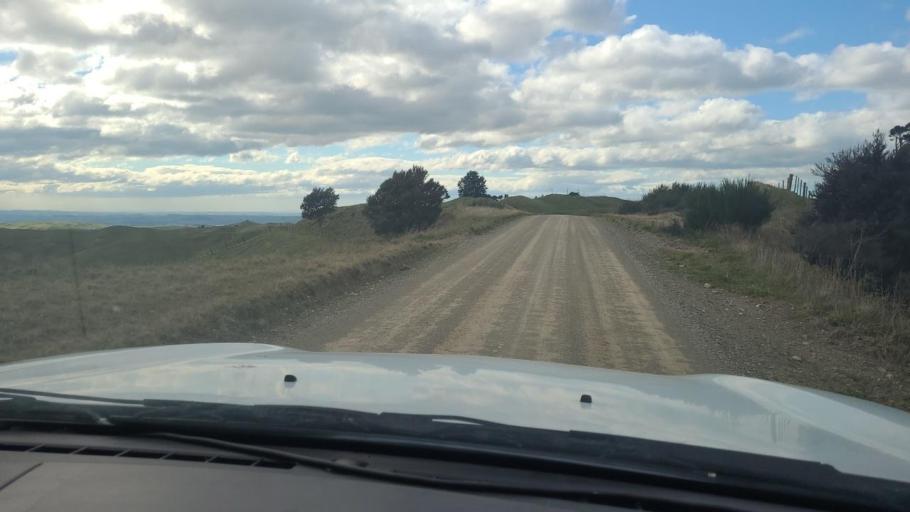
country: NZ
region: Hawke's Bay
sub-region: Hastings District
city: Hastings
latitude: -39.6863
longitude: 176.4657
